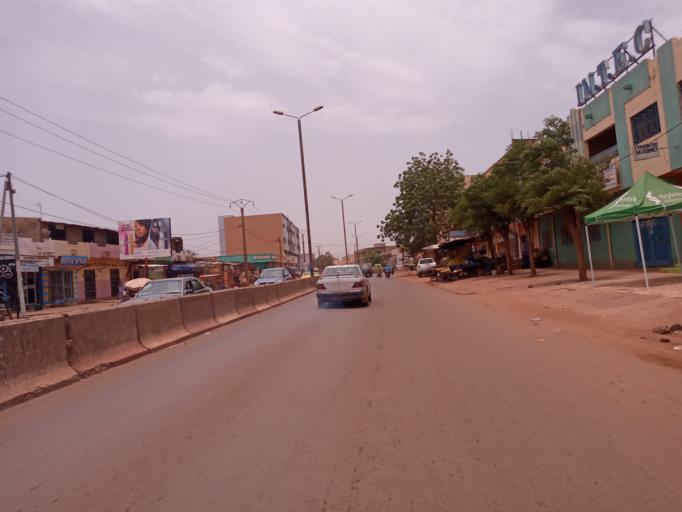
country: ML
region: Bamako
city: Bamako
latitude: 12.5910
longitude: -8.0201
